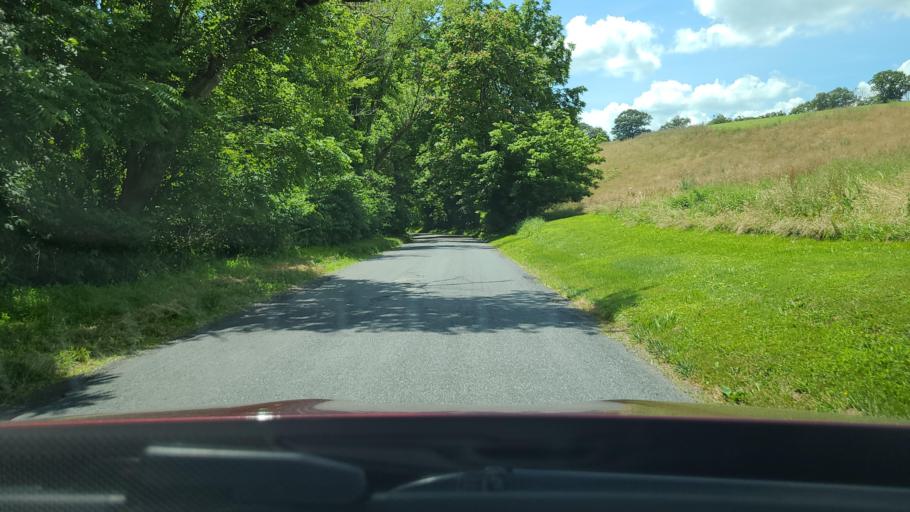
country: US
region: Maryland
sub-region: Montgomery County
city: Damascus
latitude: 39.2691
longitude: -77.2378
